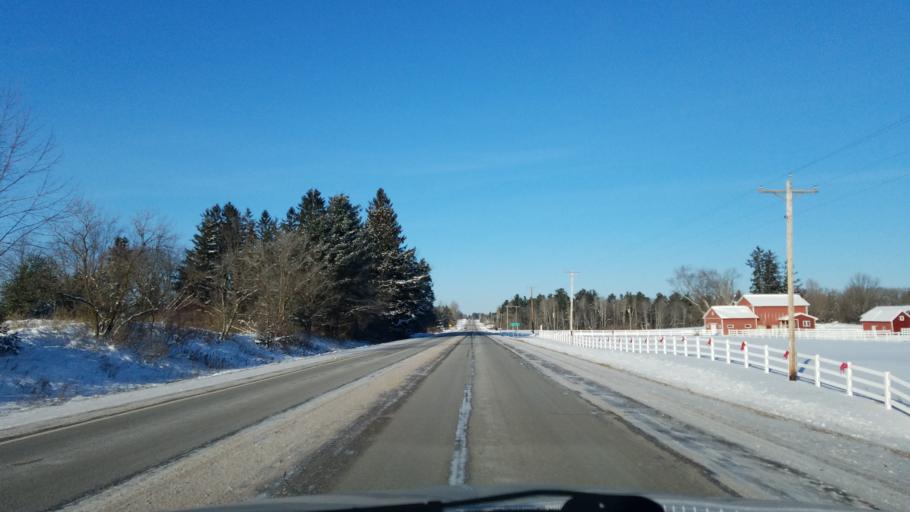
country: US
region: Wisconsin
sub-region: Barron County
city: Cumberland
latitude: 45.5065
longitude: -92.0523
